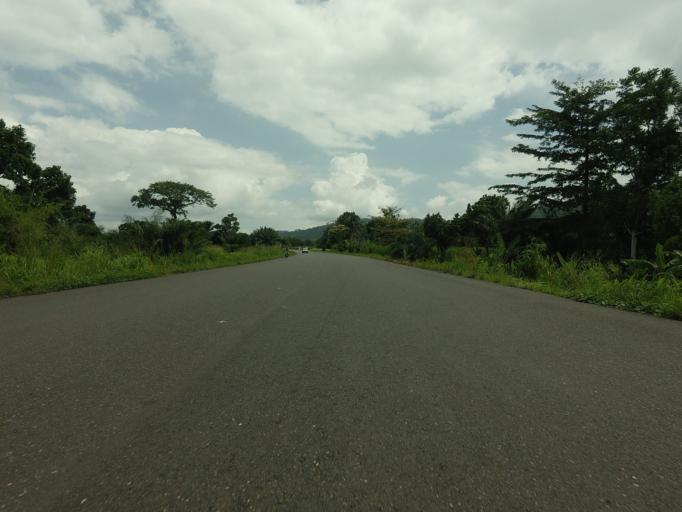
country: GH
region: Volta
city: Ho
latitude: 6.5392
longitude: 0.2354
